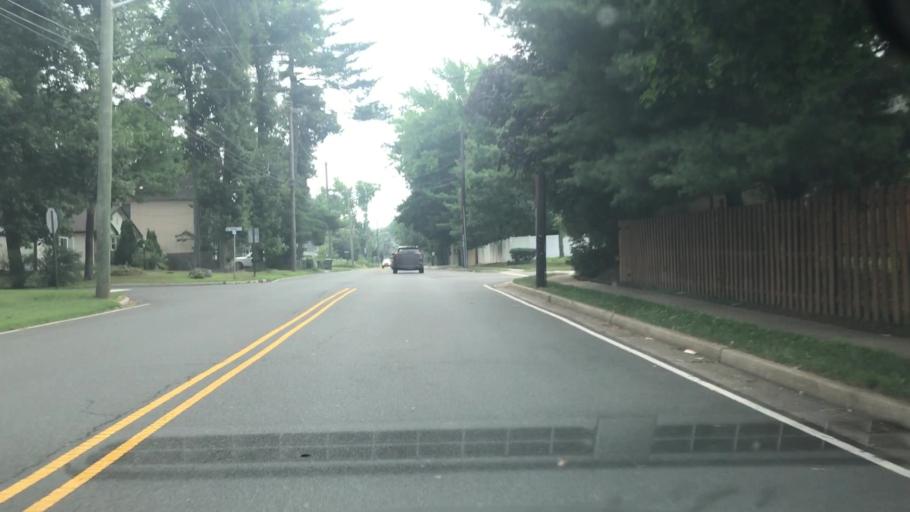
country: US
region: New Jersey
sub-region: Middlesex County
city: Iselin
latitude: 40.6024
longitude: -74.3467
